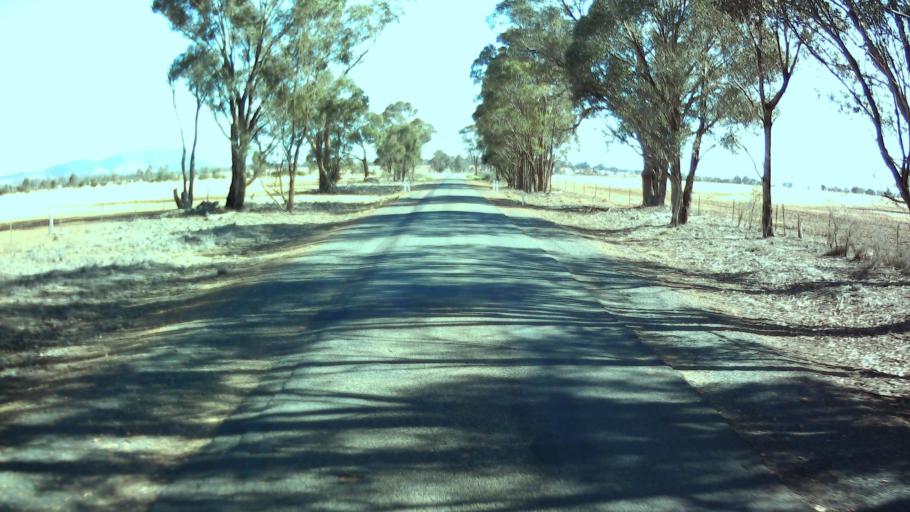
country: AU
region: New South Wales
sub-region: Weddin
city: Grenfell
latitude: -33.8017
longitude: 147.9556
